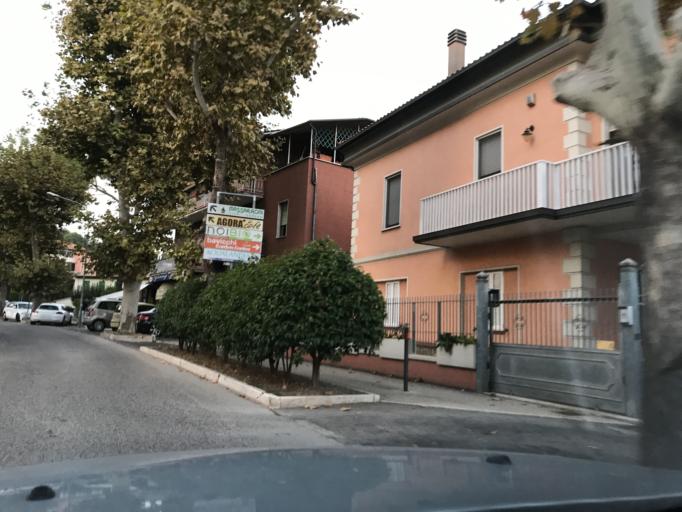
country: IT
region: Umbria
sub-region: Provincia di Perugia
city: Via Lippia
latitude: 43.0906
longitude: 12.4456
